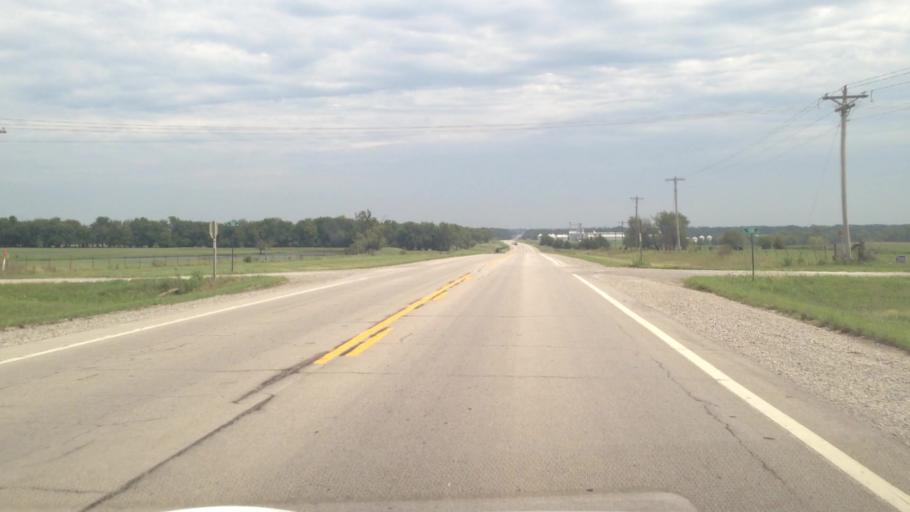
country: US
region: Kansas
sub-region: Crawford County
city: Girard
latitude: 37.5144
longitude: -94.9248
